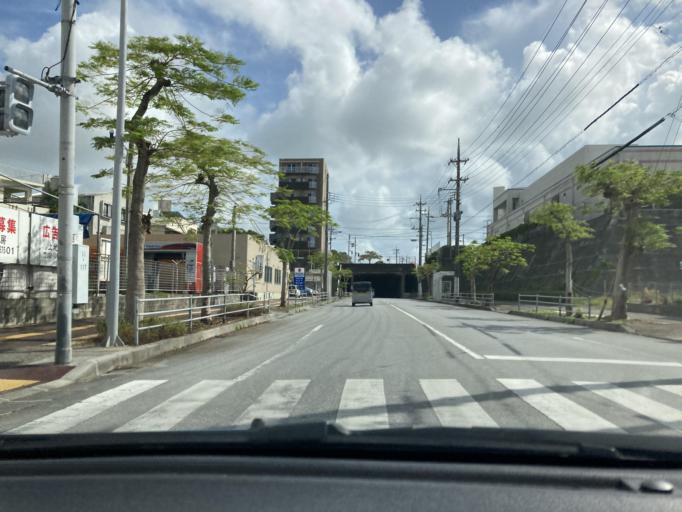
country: JP
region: Okinawa
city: Tomigusuku
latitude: 26.1875
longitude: 127.6732
